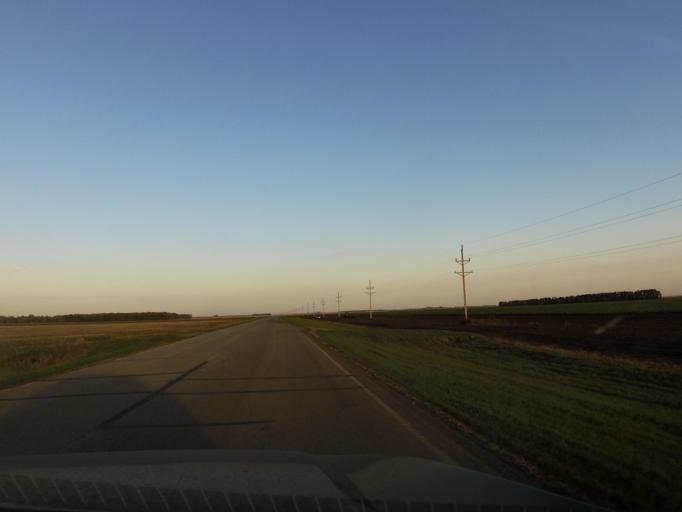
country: CA
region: Manitoba
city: Altona
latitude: 48.9635
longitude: -97.6565
